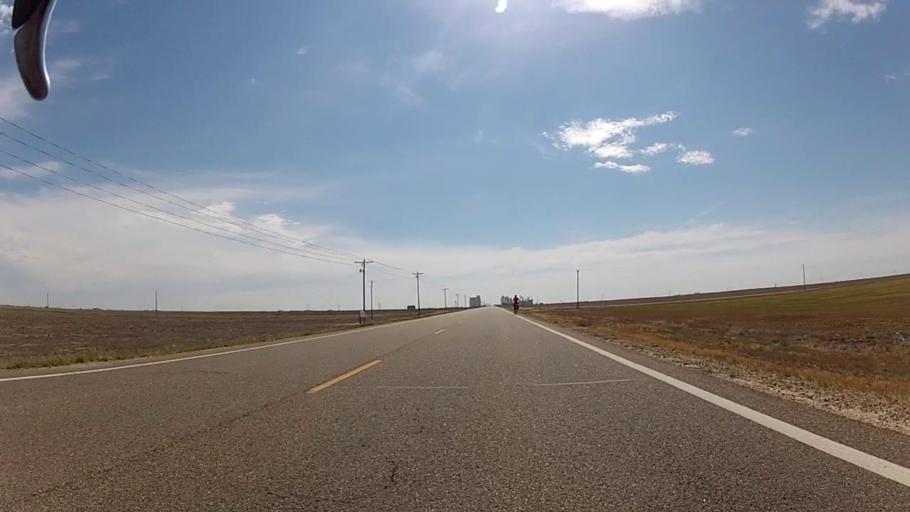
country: US
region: Kansas
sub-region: Grant County
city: Ulysses
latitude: 37.5618
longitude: -101.2567
